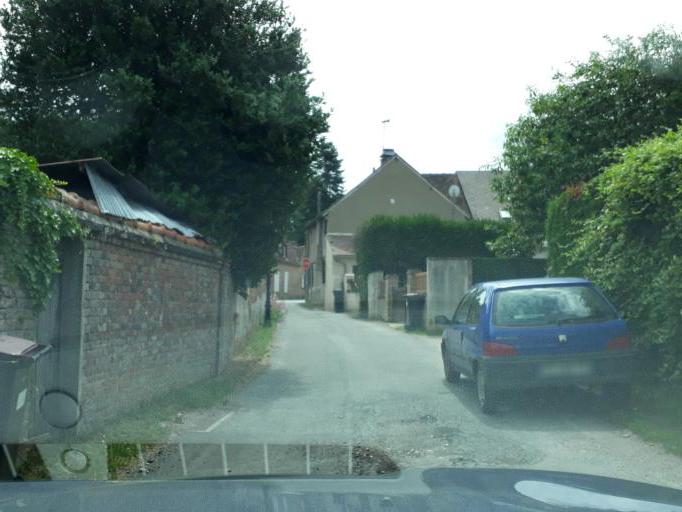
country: FR
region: Centre
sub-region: Departement du Loir-et-Cher
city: Chaumont-sur-Tharonne
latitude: 47.6119
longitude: 1.9050
